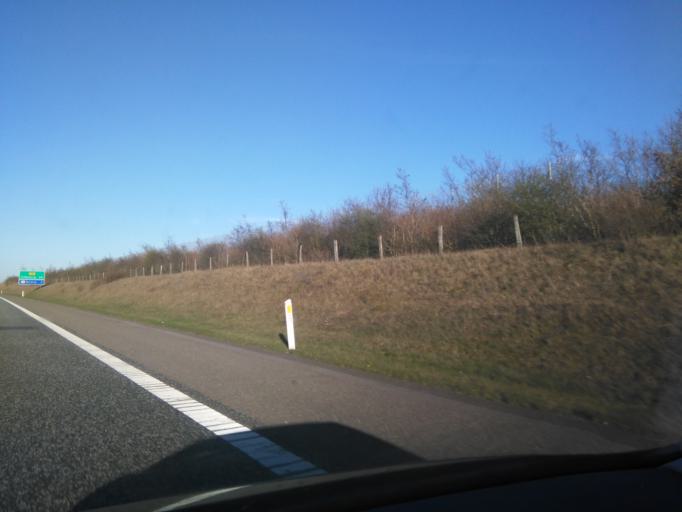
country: DK
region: Central Jutland
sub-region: Ikast-Brande Kommune
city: Ikast
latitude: 56.1227
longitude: 9.1899
